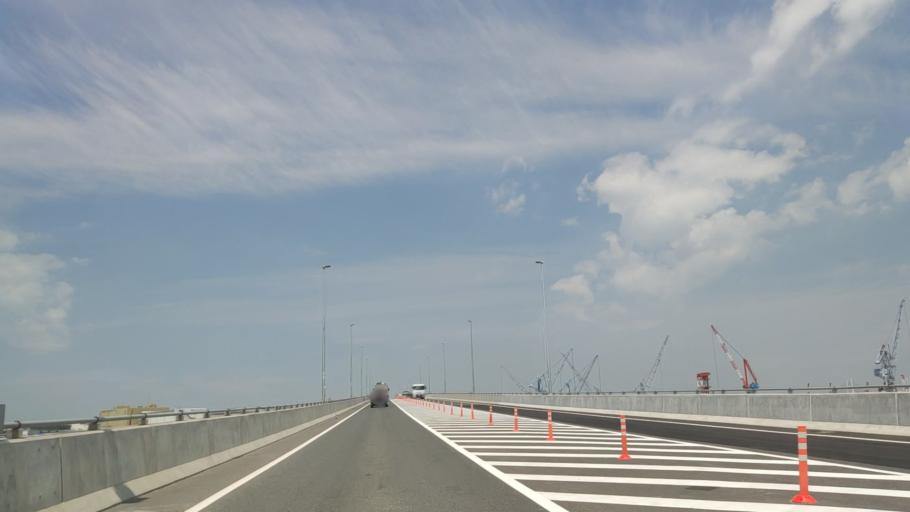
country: JP
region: Kanagawa
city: Yokohama
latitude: 35.4097
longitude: 139.6838
